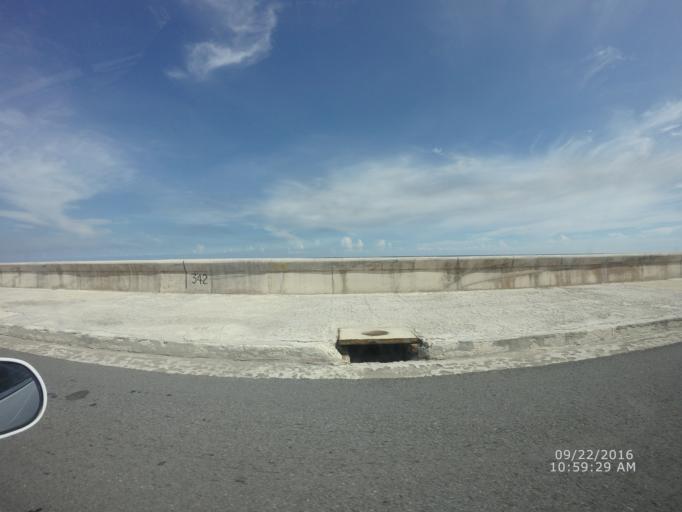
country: CU
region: La Habana
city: Havana
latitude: 23.1465
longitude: -82.3891
